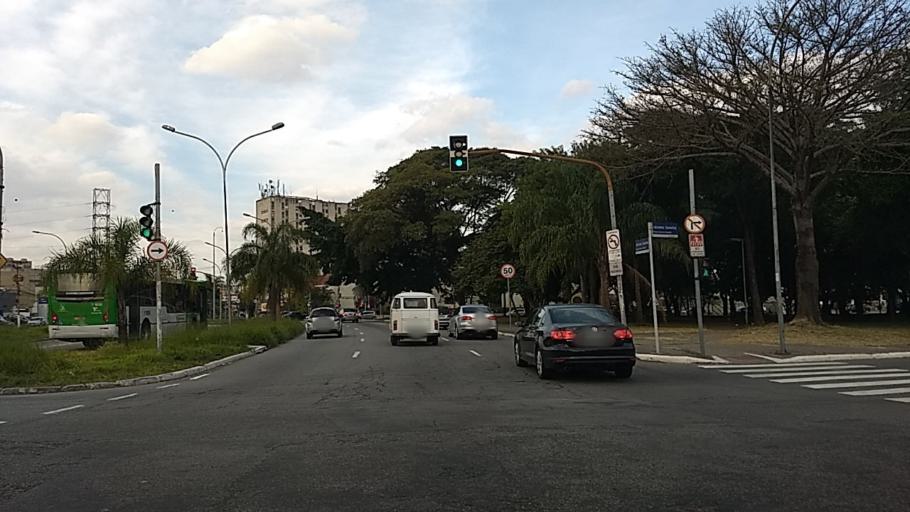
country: BR
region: Sao Paulo
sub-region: Sao Paulo
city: Sao Paulo
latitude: -23.5151
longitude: -46.6989
